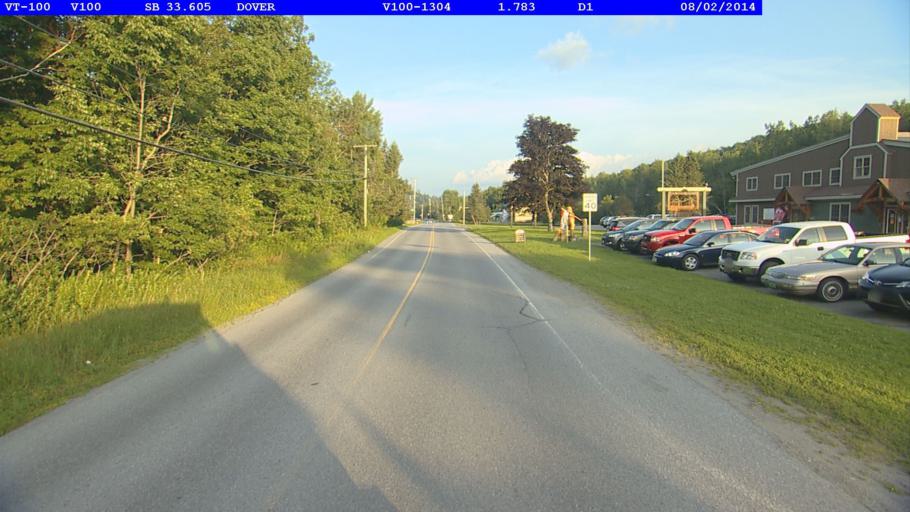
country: US
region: Vermont
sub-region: Windham County
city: Dover
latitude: 42.9444
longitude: -72.8628
